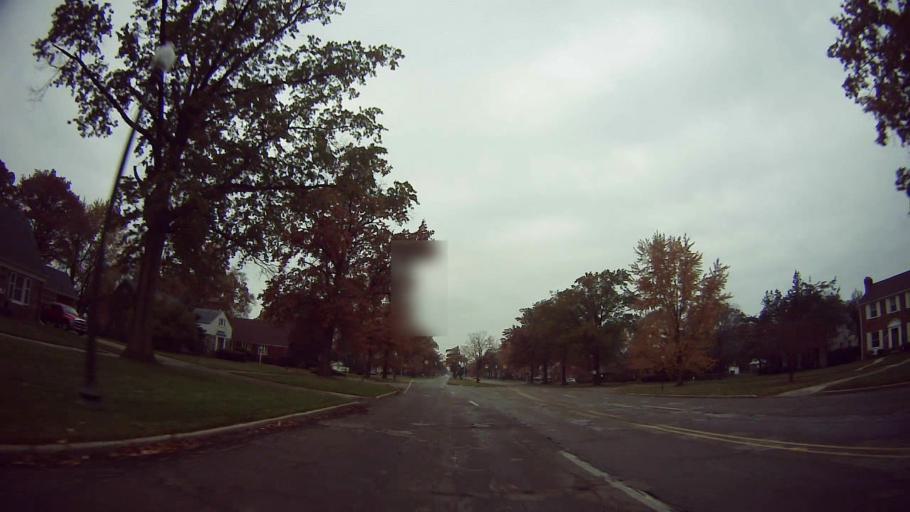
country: US
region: Michigan
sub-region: Oakland County
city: Oak Park
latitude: 42.4347
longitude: -83.1708
